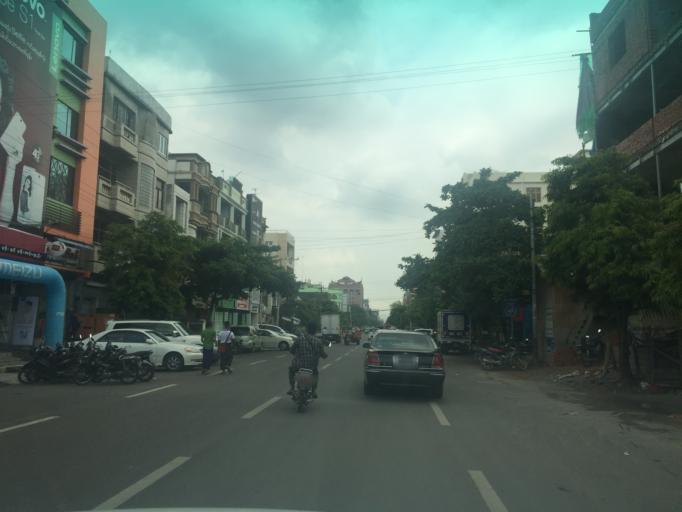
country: MM
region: Mandalay
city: Mandalay
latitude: 21.9700
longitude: 96.0788
